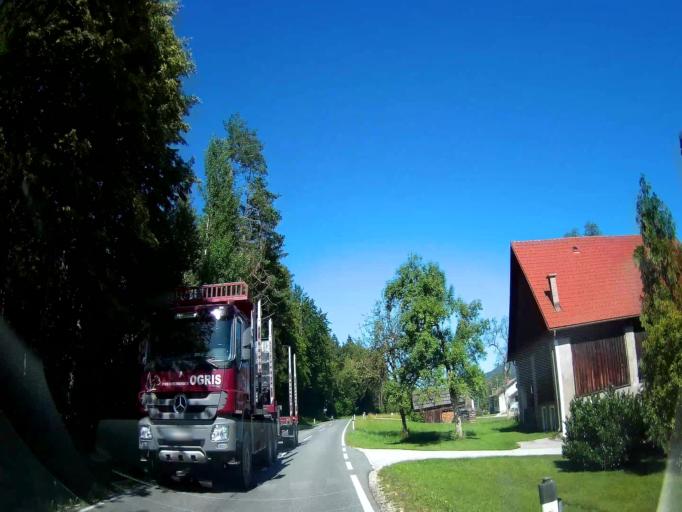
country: AT
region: Carinthia
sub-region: Politischer Bezirk Klagenfurt Land
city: Ebenthal
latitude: 46.5389
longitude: 14.3773
